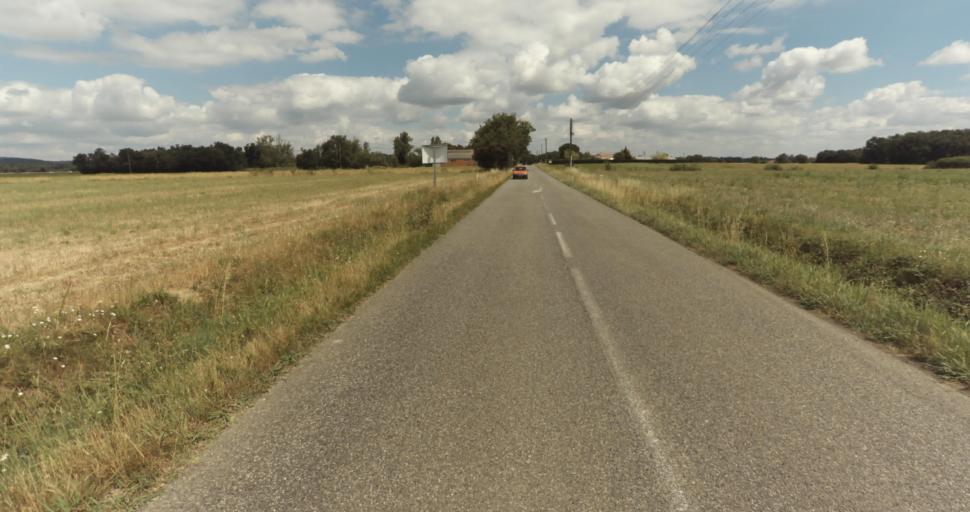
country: FR
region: Midi-Pyrenees
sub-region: Departement de la Haute-Garonne
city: Fontenilles
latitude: 43.5588
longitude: 1.1933
